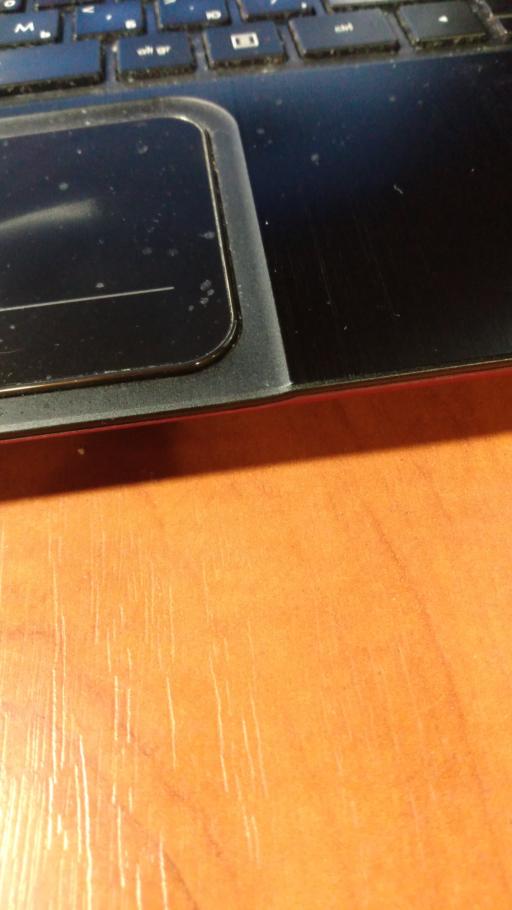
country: RU
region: Republic of Karelia
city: Pudozh
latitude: 62.1267
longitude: 37.5538
